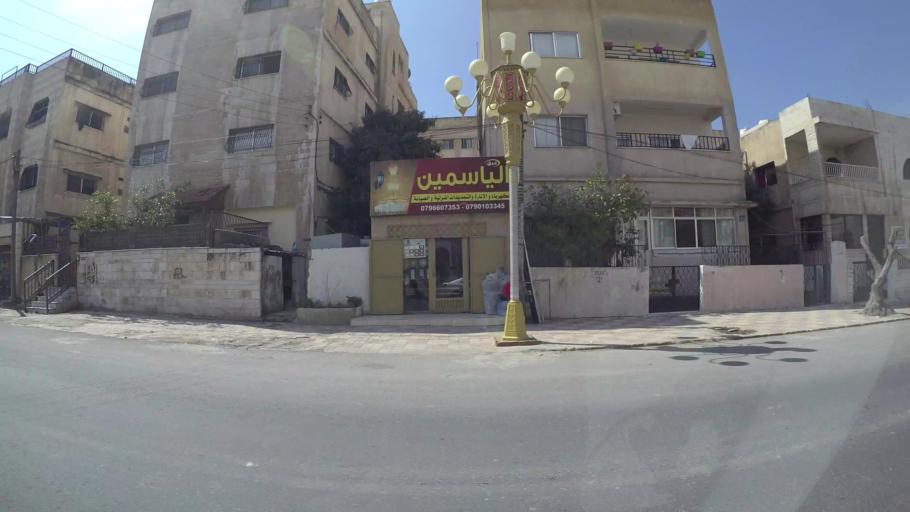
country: JO
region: Amman
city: Al Bunayyat ash Shamaliyah
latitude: 31.9283
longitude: 35.9052
